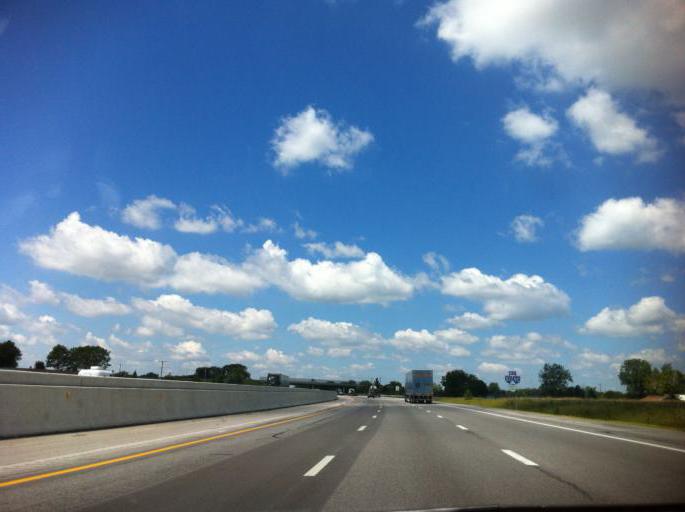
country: US
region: Ohio
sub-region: Ottawa County
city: Elmore
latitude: 41.4639
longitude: -83.2950
